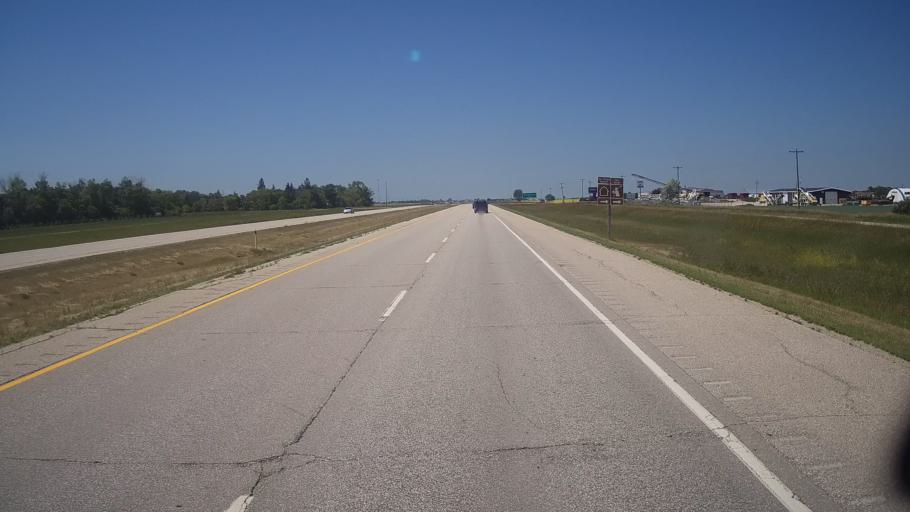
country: CA
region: Manitoba
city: Stonewall
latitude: 49.9900
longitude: -97.2705
